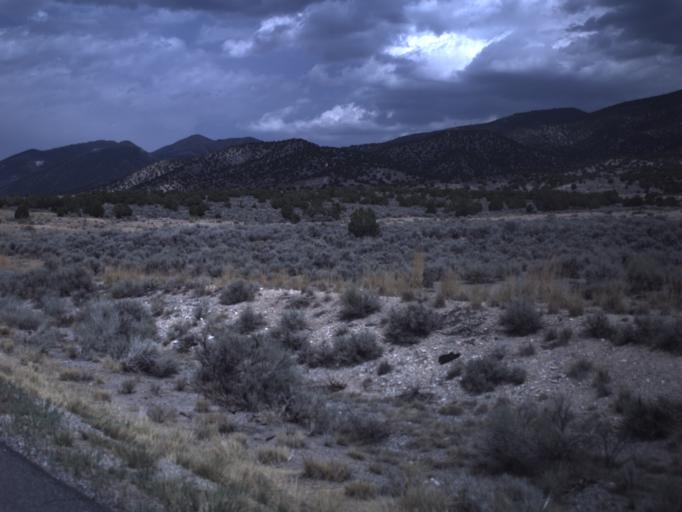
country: US
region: Utah
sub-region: Tooele County
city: Tooele
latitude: 40.3094
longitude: -112.2808
